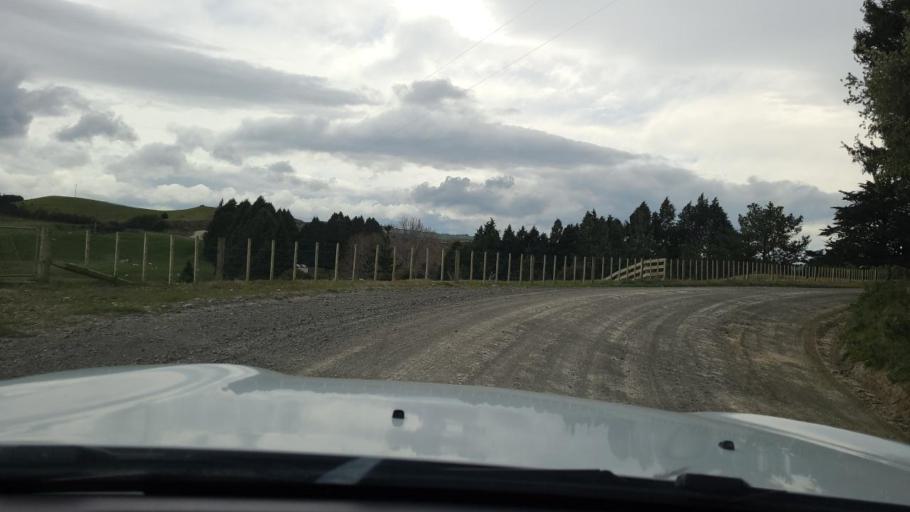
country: NZ
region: Hawke's Bay
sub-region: Napier City
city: Napier
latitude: -39.3144
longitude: 176.8357
